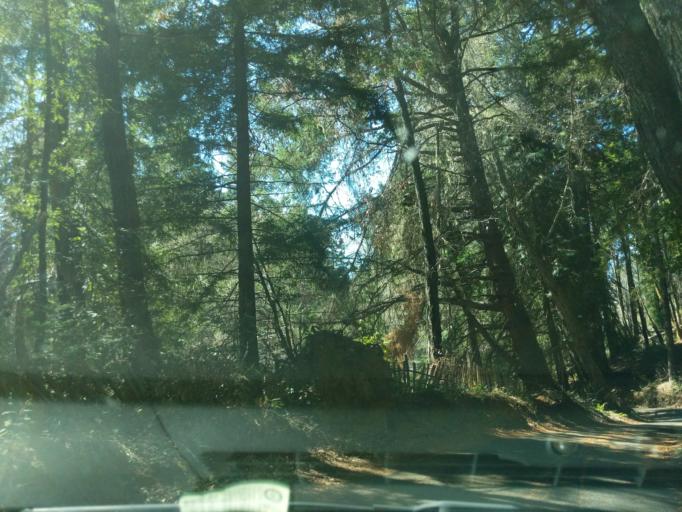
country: US
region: California
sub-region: Sonoma County
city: Monte Rio
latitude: 38.5236
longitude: -123.2310
